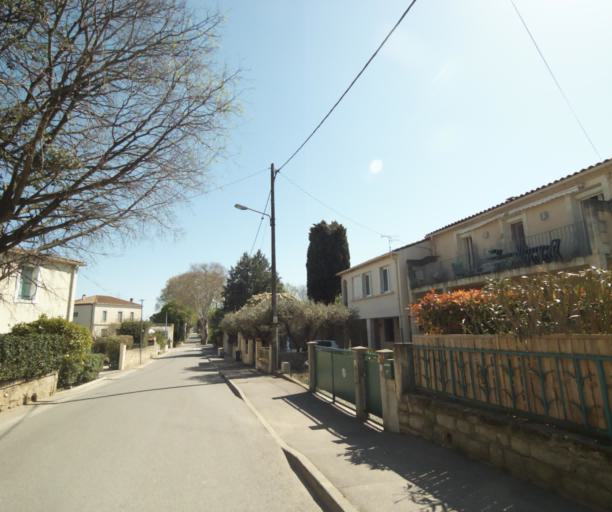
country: FR
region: Languedoc-Roussillon
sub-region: Departement de l'Herault
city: Saint-Drezery
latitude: 43.7321
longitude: 3.9812
